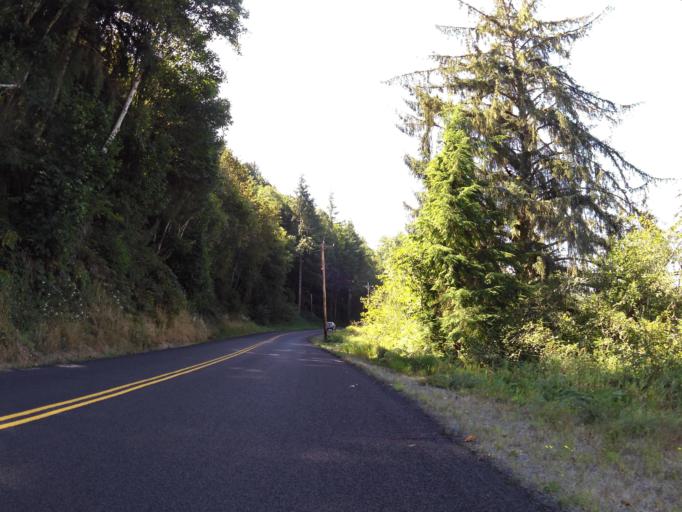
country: US
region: Washington
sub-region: Wahkiakum County
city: Cathlamet
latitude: 46.1941
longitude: -123.5723
